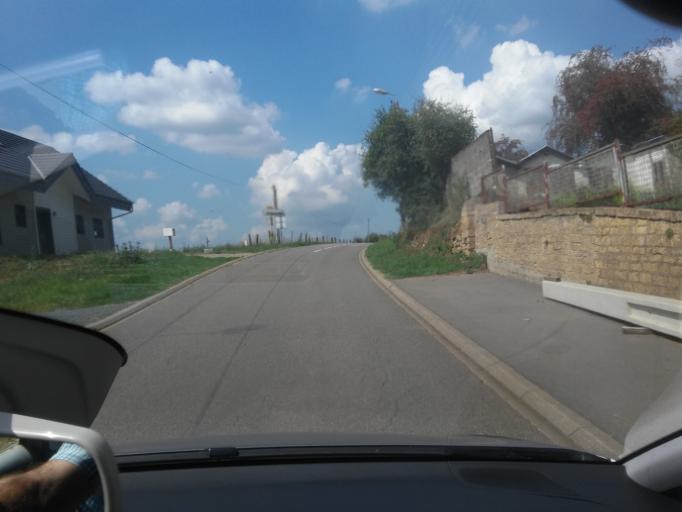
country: BE
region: Wallonia
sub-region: Province du Luxembourg
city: Rouvroy
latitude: 49.4941
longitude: 5.4983
